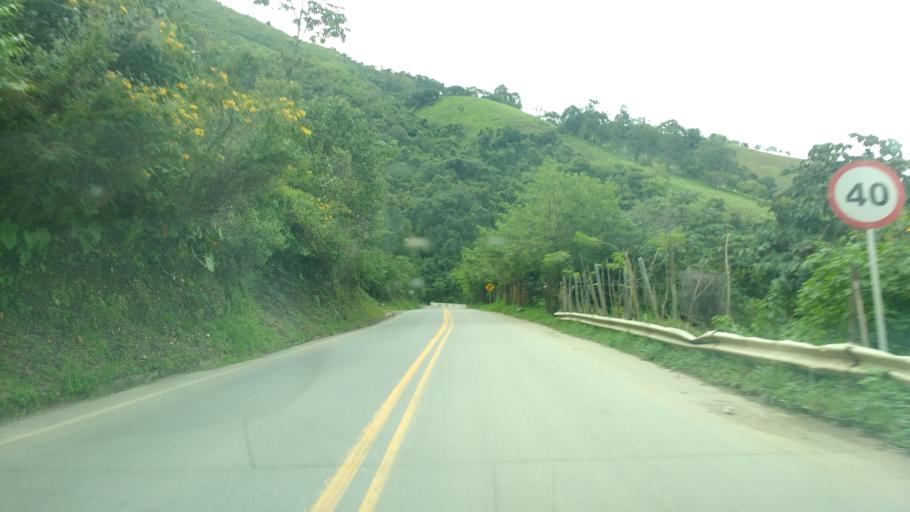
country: CO
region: Antioquia
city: Amaga
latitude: 6.0536
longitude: -75.7265
